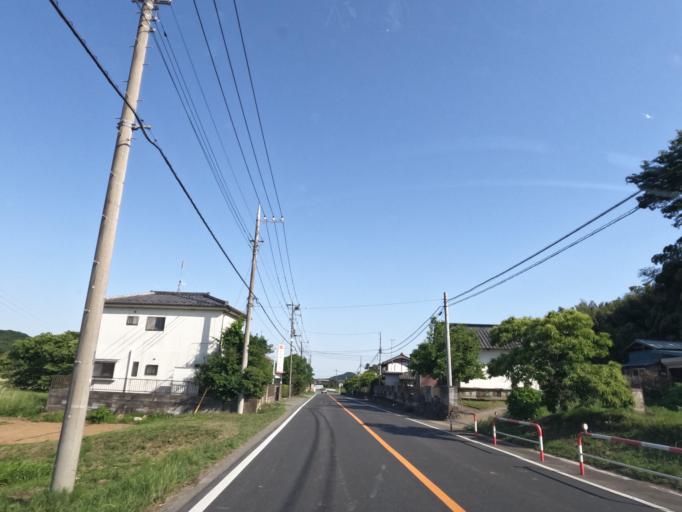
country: JP
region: Saitama
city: Ogawa
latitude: 36.0763
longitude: 139.2926
